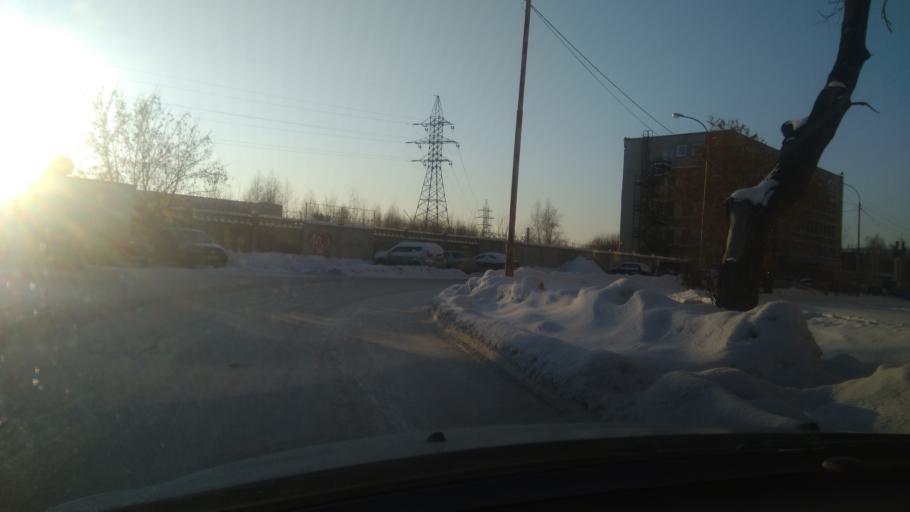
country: RU
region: Sverdlovsk
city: Yekaterinburg
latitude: 56.8815
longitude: 60.5662
